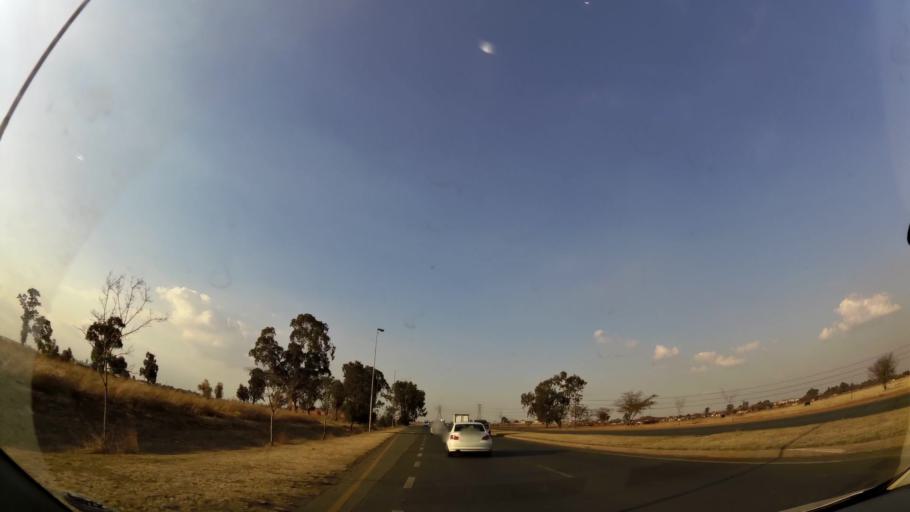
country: ZA
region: Gauteng
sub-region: Ekurhuleni Metropolitan Municipality
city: Germiston
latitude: -26.3383
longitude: 28.2265
